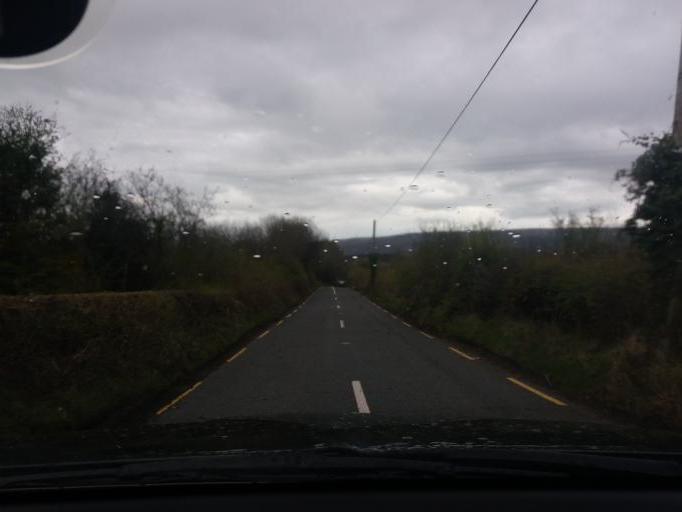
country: IE
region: Ulster
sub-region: An Cabhan
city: Ballyconnell
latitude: 54.1567
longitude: -7.7419
